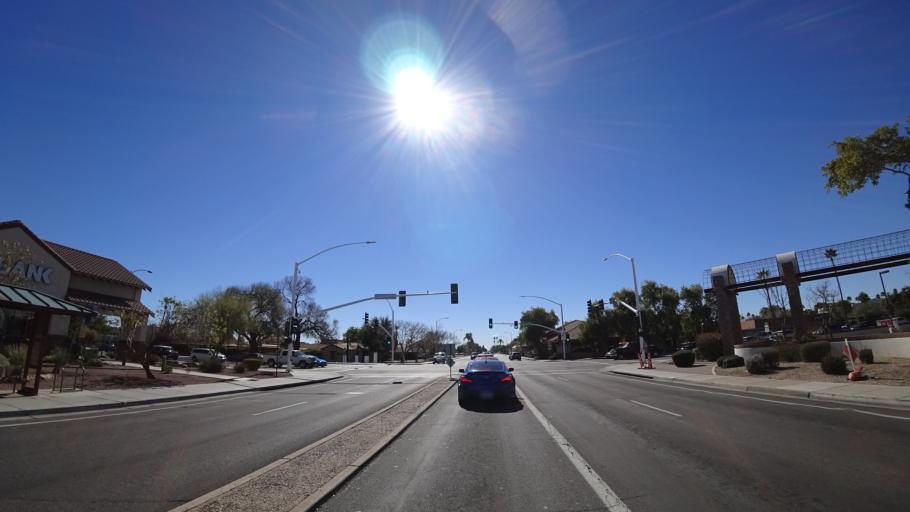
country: US
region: Arizona
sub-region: Maricopa County
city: Scottsdale
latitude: 33.4954
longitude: -111.9176
